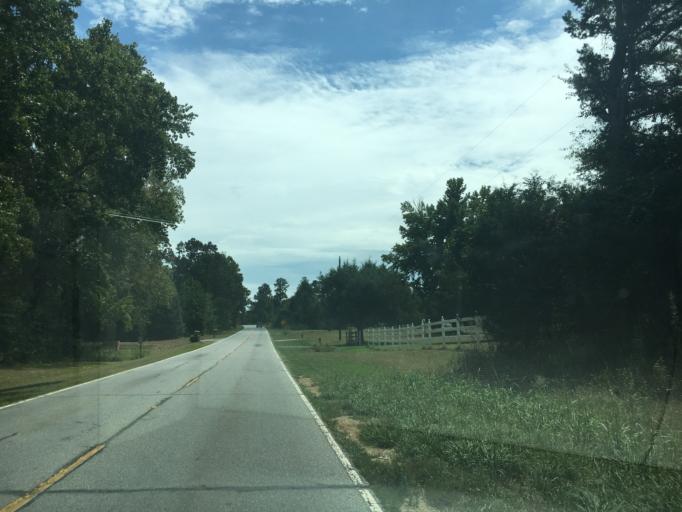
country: US
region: South Carolina
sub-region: Laurens County
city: Laurens
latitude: 34.5842
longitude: -82.0990
